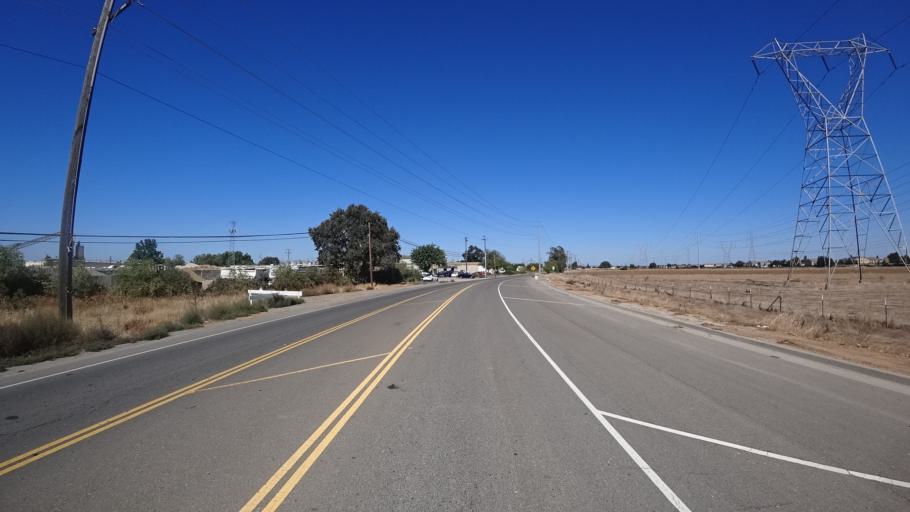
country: US
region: California
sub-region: Sacramento County
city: Elk Grove
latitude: 38.3877
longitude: -121.3527
